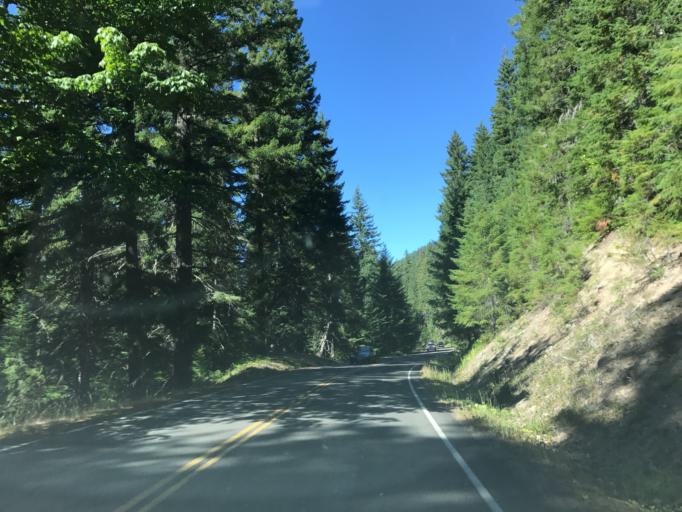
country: US
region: Washington
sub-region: Pierce County
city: Buckley
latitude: 46.7448
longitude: -121.6196
